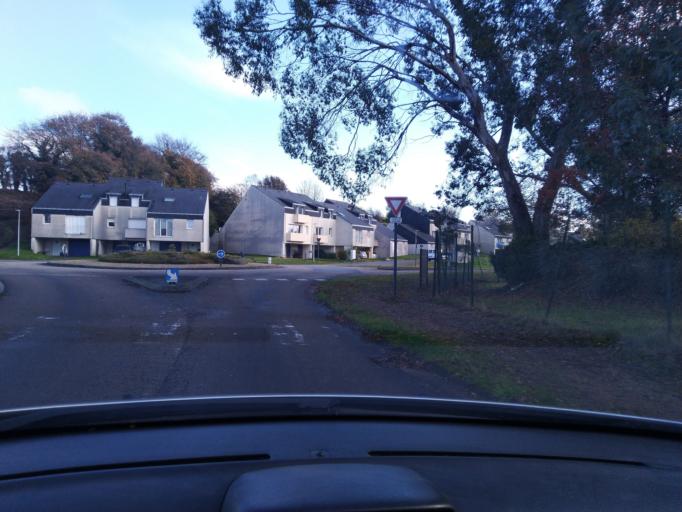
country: FR
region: Brittany
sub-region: Departement du Finistere
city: Guerlesquin
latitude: 48.5125
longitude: -3.5851
